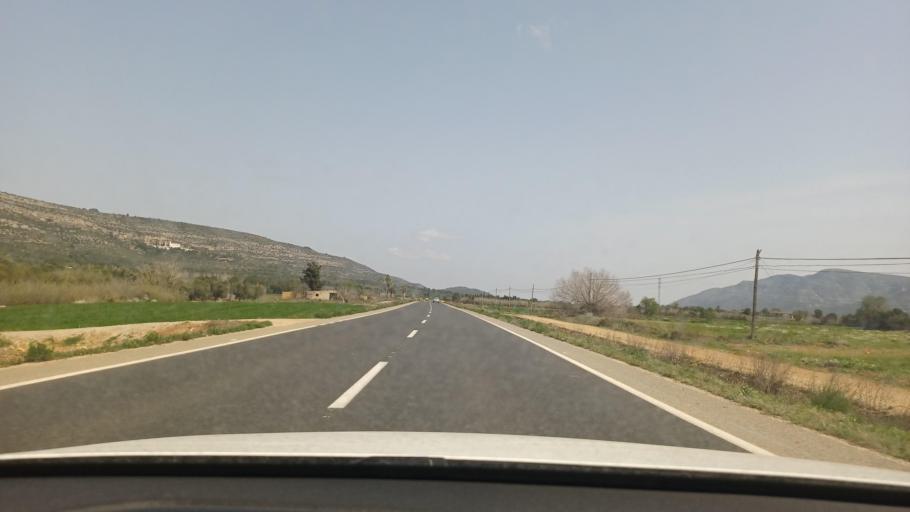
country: ES
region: Catalonia
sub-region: Provincia de Tarragona
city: Ulldecona
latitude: 40.6138
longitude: 0.4655
